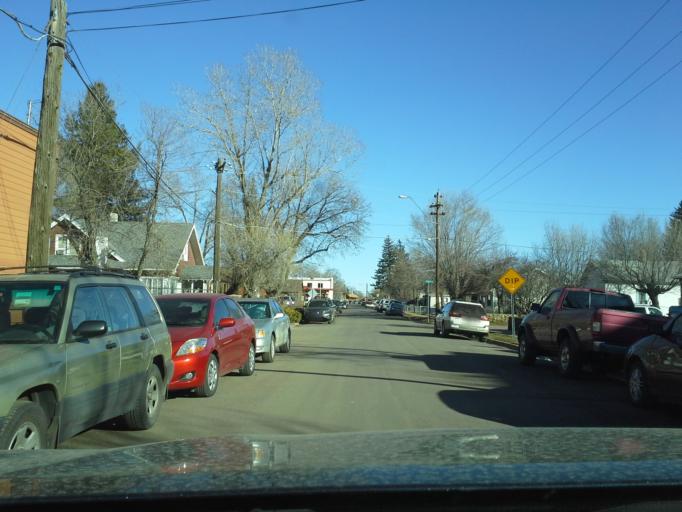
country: US
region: Arizona
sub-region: Coconino County
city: Flagstaff
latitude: 35.1962
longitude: -111.6527
